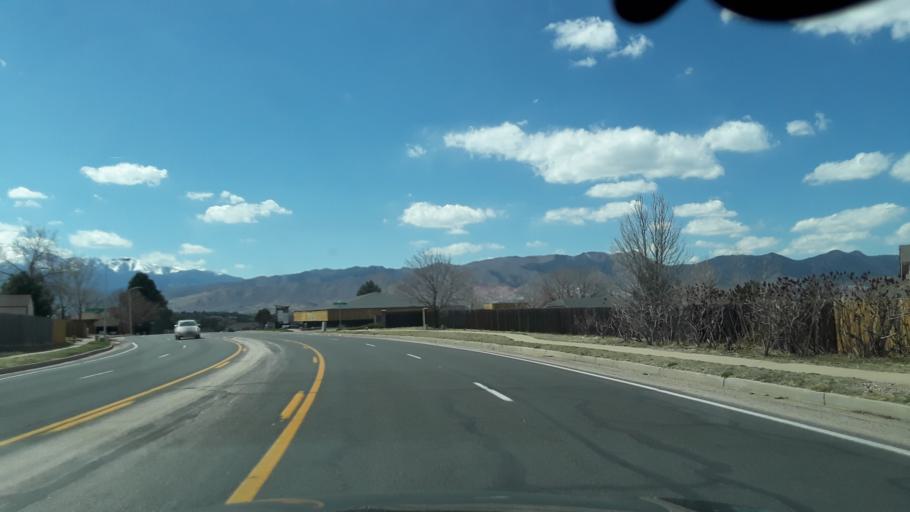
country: US
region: Colorado
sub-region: El Paso County
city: Colorado Springs
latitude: 38.9158
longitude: -104.7821
